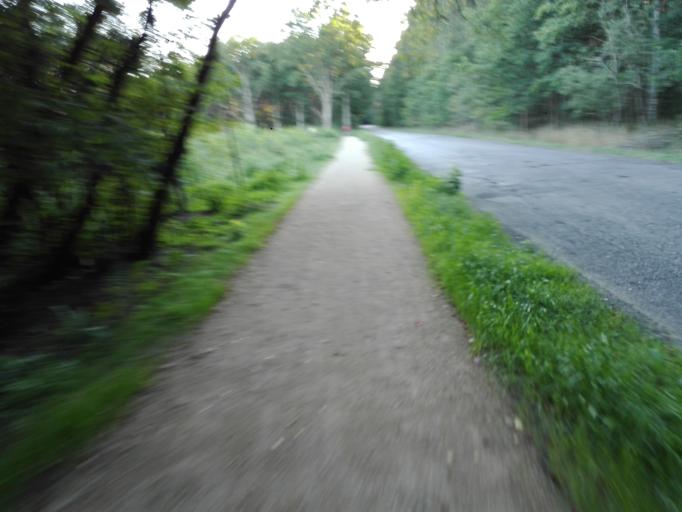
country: PL
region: West Pomeranian Voivodeship
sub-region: Powiat policki
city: Dobra
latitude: 53.4810
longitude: 14.3684
